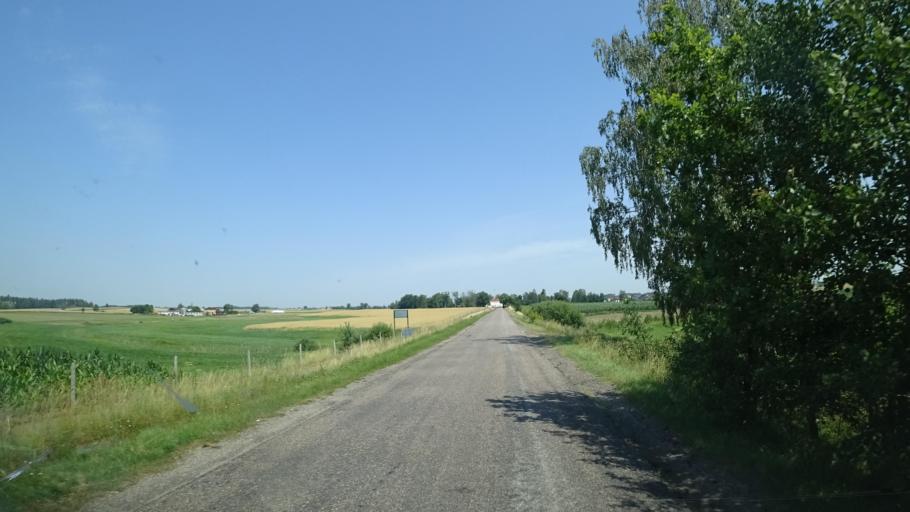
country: PL
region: Pomeranian Voivodeship
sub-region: Powiat chojnicki
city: Brusy
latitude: 53.8765
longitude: 17.6288
